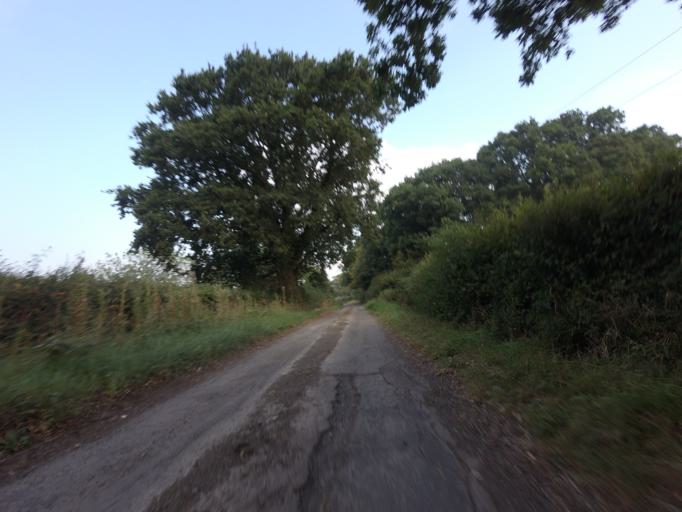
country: GB
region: England
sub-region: Kent
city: Tenterden
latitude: 51.1125
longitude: 0.7768
